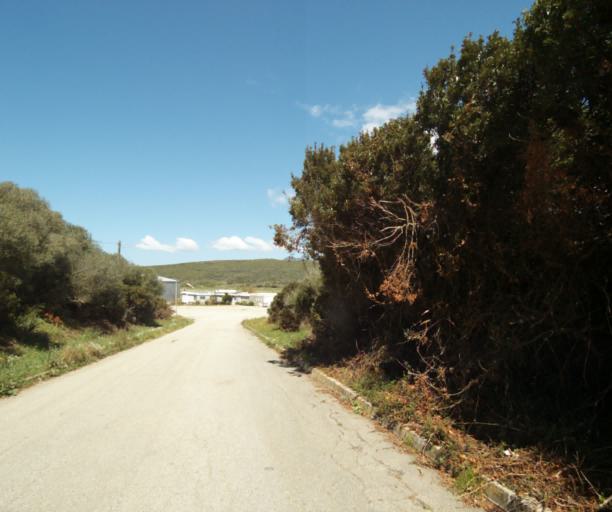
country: FR
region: Corsica
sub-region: Departement de la Corse-du-Sud
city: Propriano
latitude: 41.6582
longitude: 8.8937
